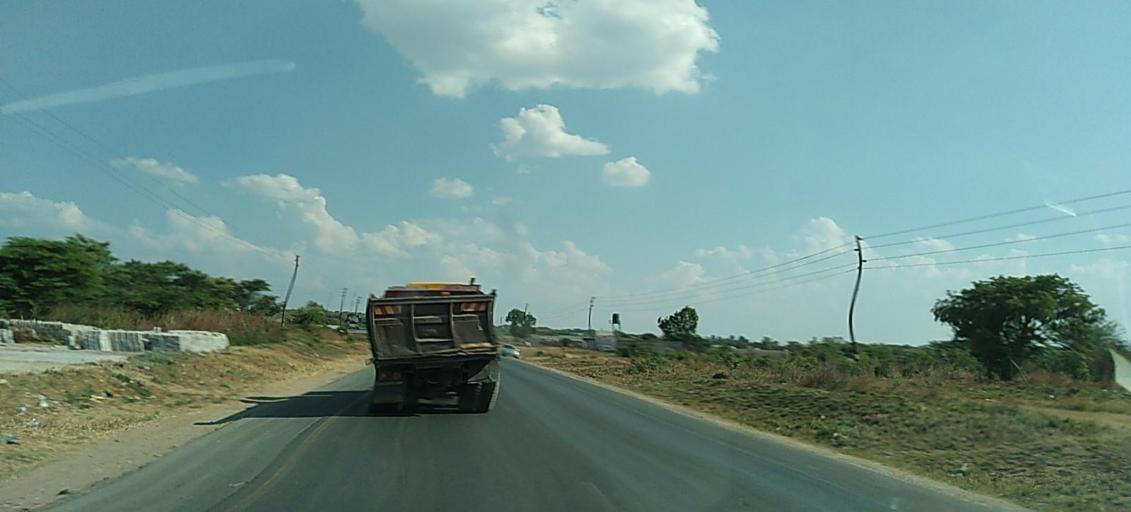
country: ZM
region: Lusaka
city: Lusaka
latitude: -15.2410
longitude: 28.2579
